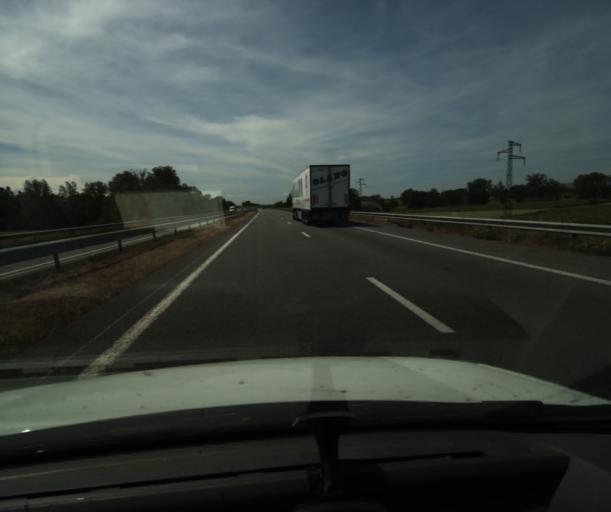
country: FR
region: Languedoc-Roussillon
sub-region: Departement de l'Aude
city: Arzens
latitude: 43.2209
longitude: 2.2057
